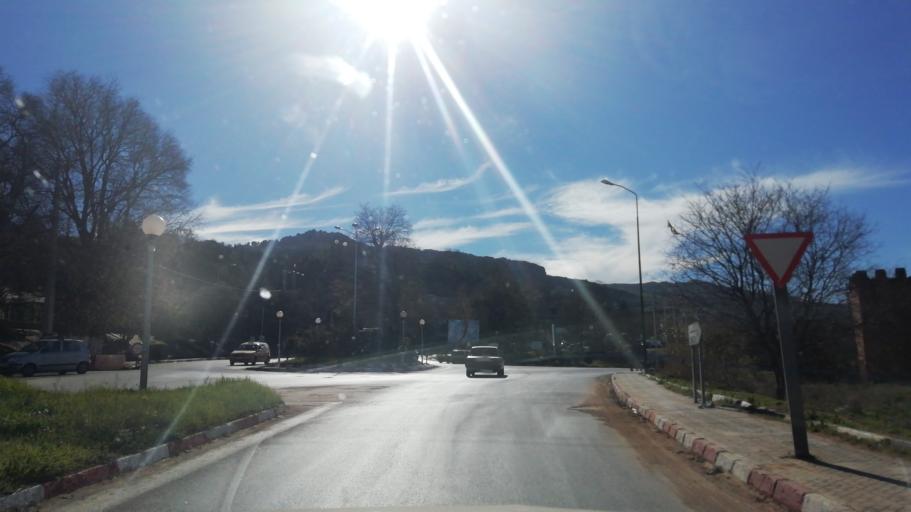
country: DZ
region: Tlemcen
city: Mansoura
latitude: 34.8653
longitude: -1.3335
